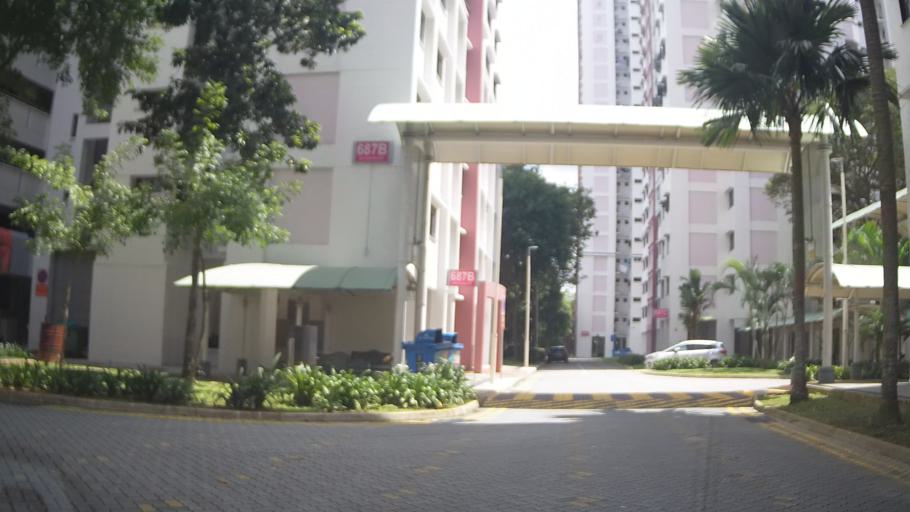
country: MY
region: Johor
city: Johor Bahru
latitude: 1.4042
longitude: 103.7504
